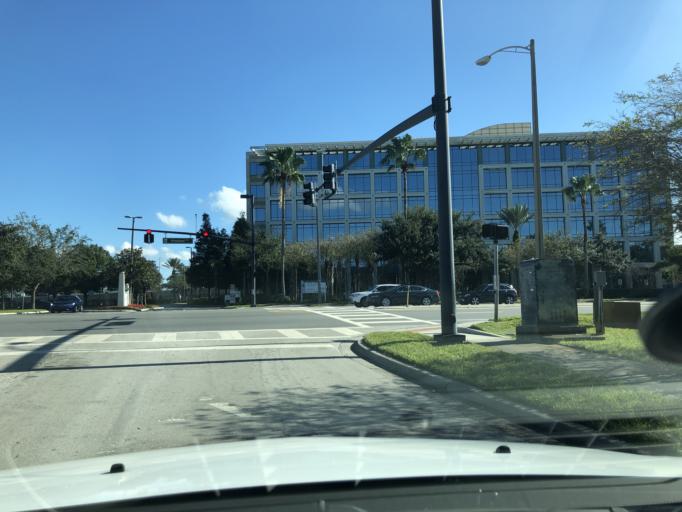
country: US
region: Florida
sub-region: Orange County
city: Oak Ridge
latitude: 28.4886
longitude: -81.4408
